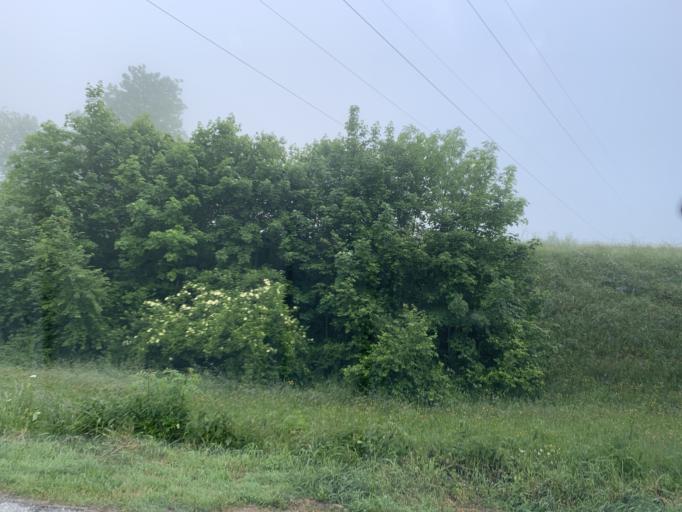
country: AT
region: Salzburg
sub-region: Politischer Bezirk Sankt Johann im Pongau
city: Forstau
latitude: 47.4022
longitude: 13.5829
